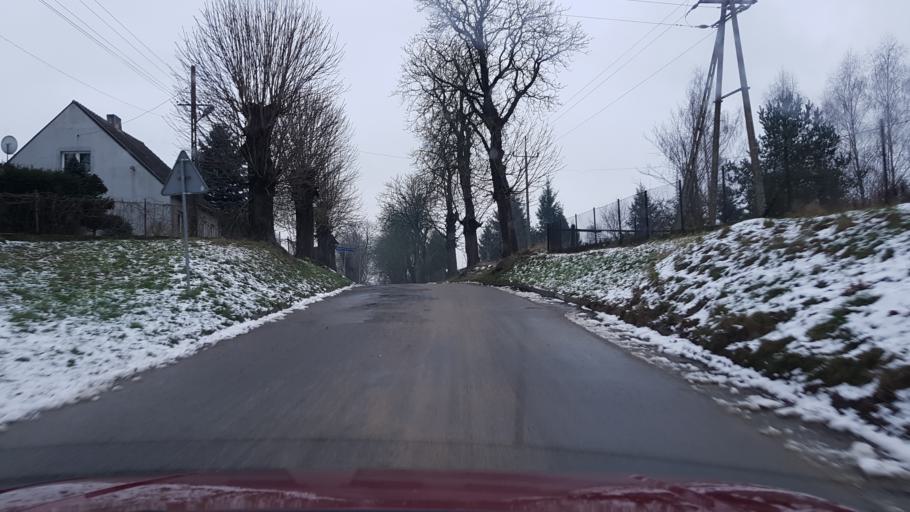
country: PL
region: West Pomeranian Voivodeship
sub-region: Powiat goleniowski
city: Mosty
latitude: 53.5222
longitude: 14.9439
